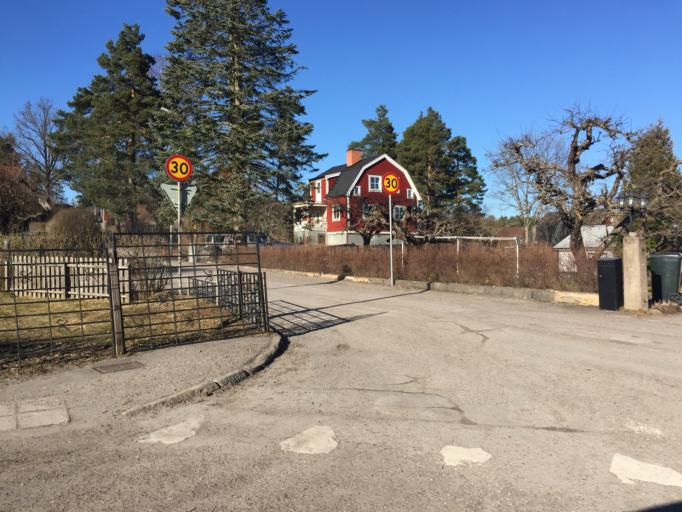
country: SE
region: OEstergoetland
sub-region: Finspangs Kommun
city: Finspang
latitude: 58.7096
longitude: 15.7574
